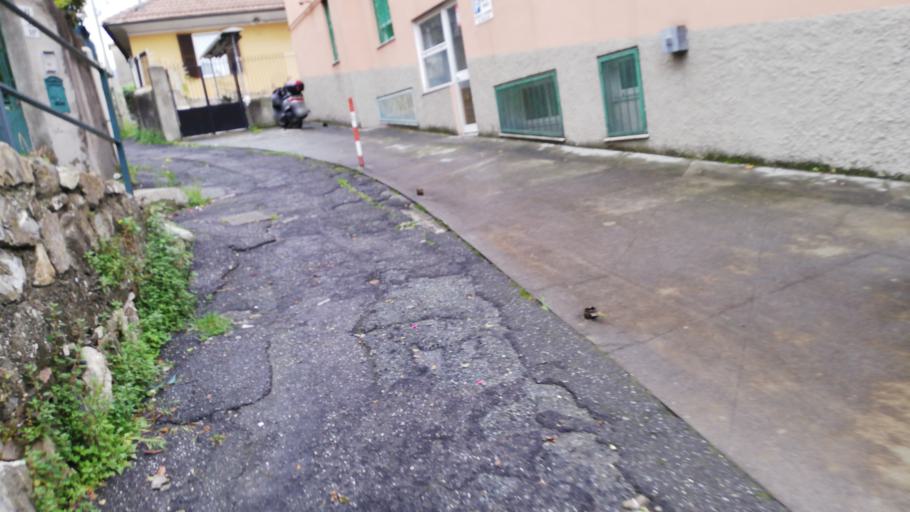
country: IT
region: Liguria
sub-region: Provincia di Genova
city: Piccarello
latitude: 44.4486
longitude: 9.0080
